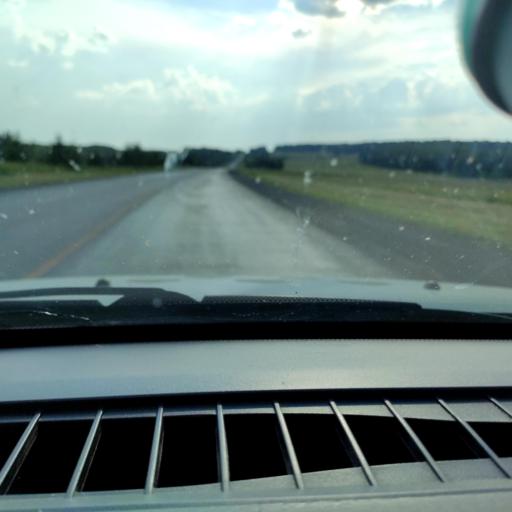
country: RU
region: Udmurtiya
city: Debesy
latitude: 57.7029
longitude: 54.0620
